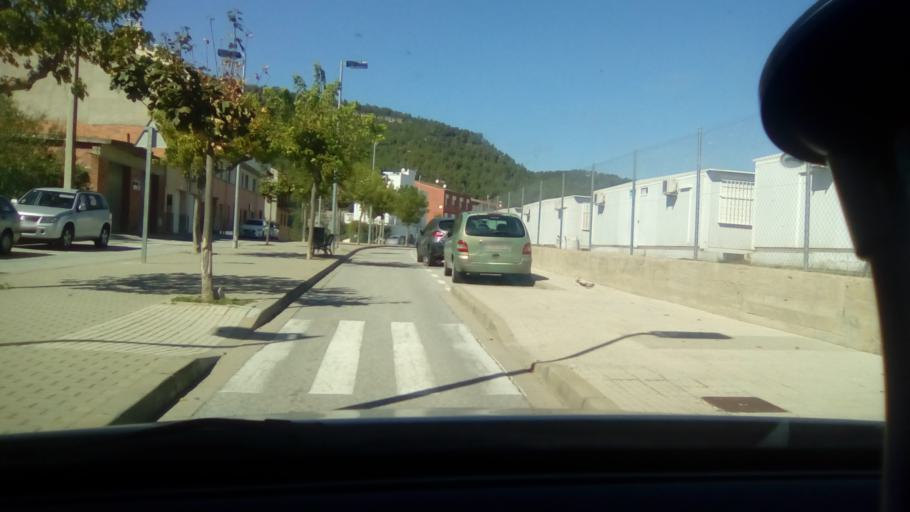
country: ES
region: Catalonia
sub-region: Provincia de Barcelona
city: Monistrol de Montserrat
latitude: 41.6315
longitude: 1.8559
